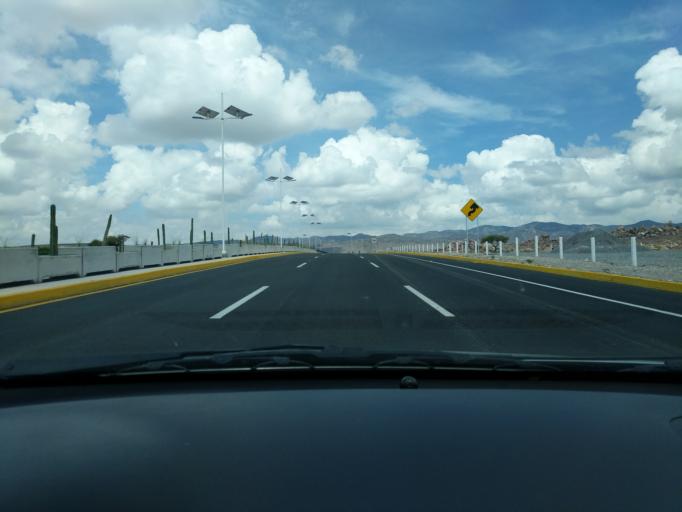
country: MX
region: San Luis Potosi
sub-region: Mexquitic de Carmona
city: Guadalupe Victoria
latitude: 22.1647
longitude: -101.0554
